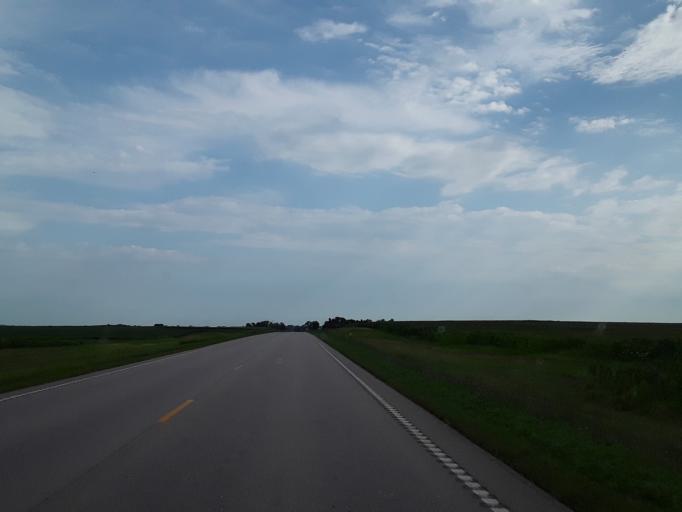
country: US
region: Nebraska
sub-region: Saunders County
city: Ashland
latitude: 41.1098
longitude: -96.4259
